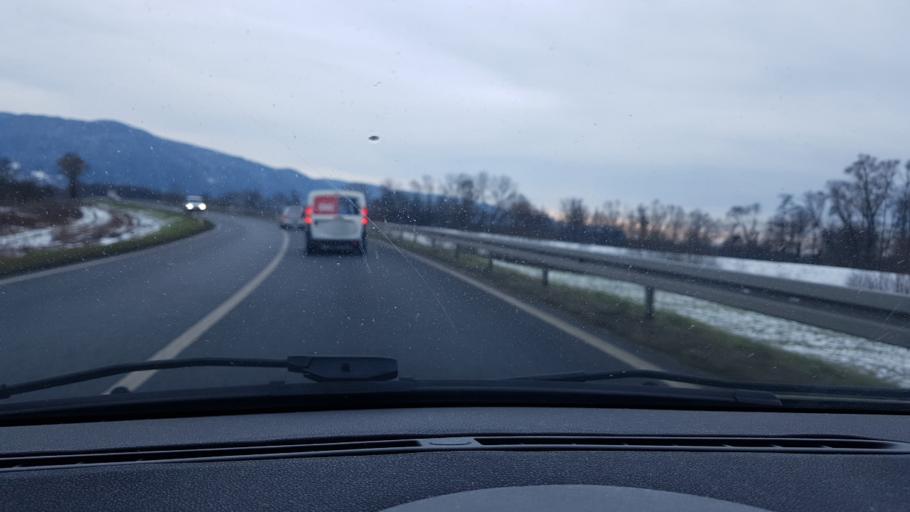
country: HR
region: Zagrebacka
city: Pojatno
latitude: 45.8964
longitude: 15.8159
